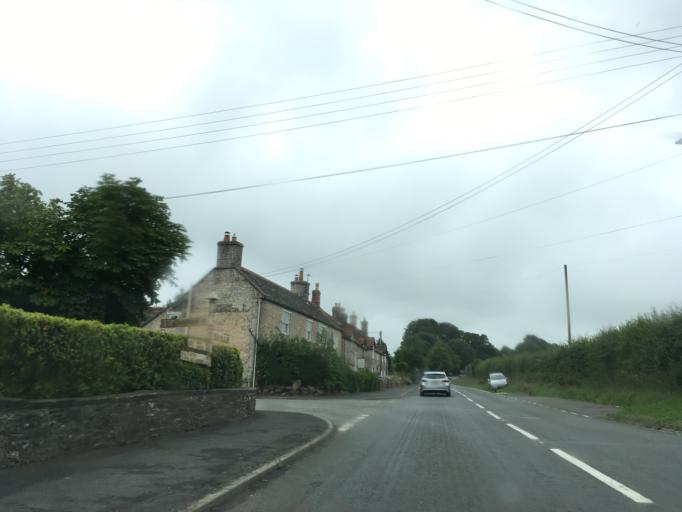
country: GB
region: England
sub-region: Bath and North East Somerset
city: East Harptree
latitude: 51.2694
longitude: -2.5865
